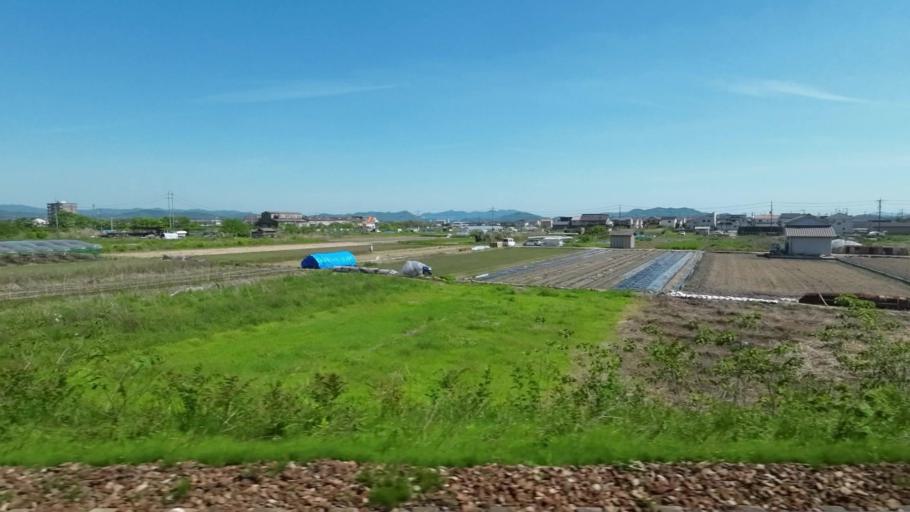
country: JP
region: Hiroshima
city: Onomichi
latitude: 34.4402
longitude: 133.2378
